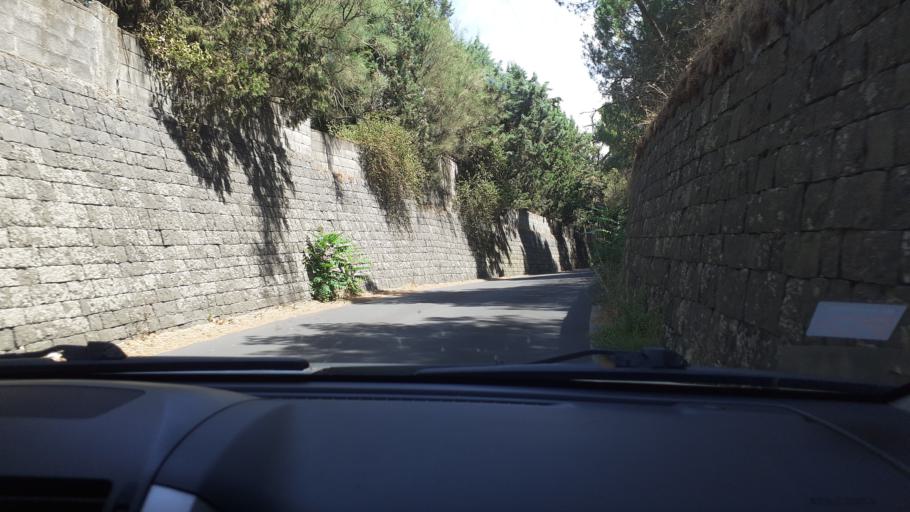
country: IT
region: Sicily
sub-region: Catania
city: Nicolosi
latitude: 37.6294
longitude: 15.0240
